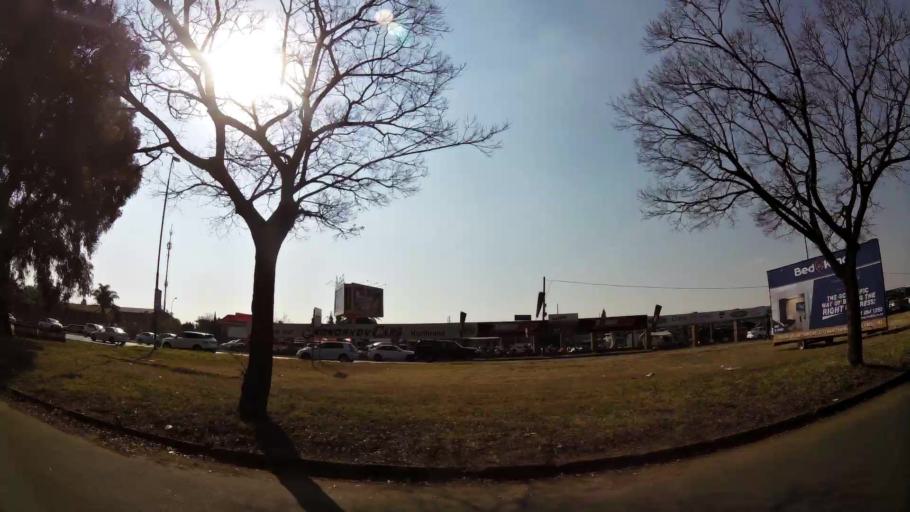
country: ZA
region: Gauteng
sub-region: Ekurhuleni Metropolitan Municipality
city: Boksburg
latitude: -26.1794
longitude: 28.2680
